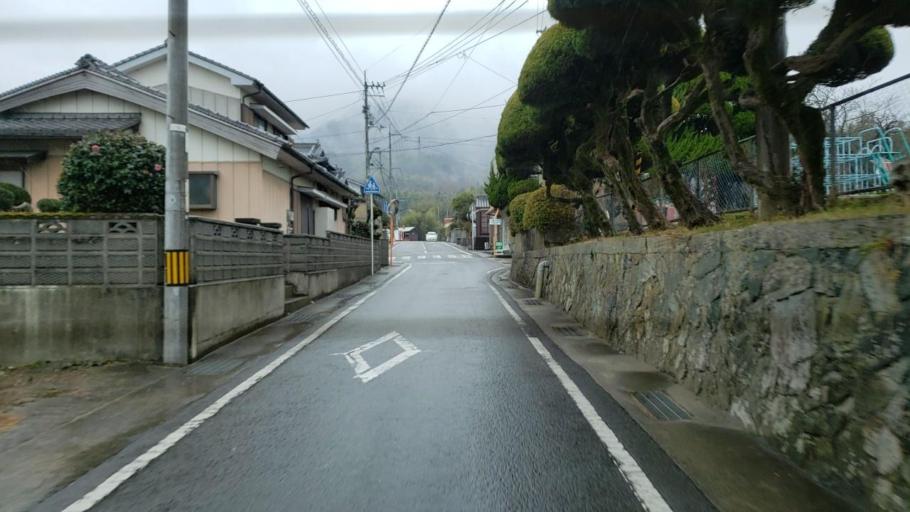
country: JP
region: Tokushima
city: Kamojimacho-jogejima
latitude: 34.0605
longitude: 134.3191
